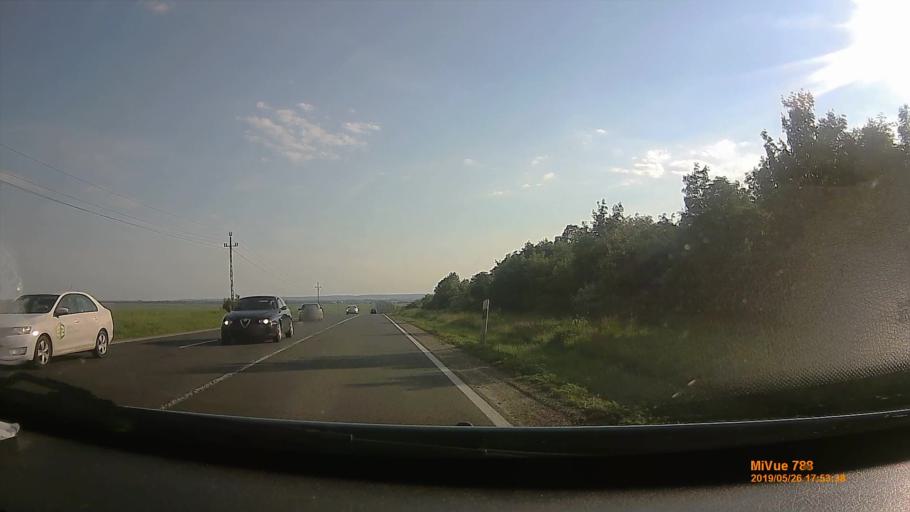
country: HU
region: Borsod-Abauj-Zemplen
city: Onga
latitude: 48.1507
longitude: 20.8948
